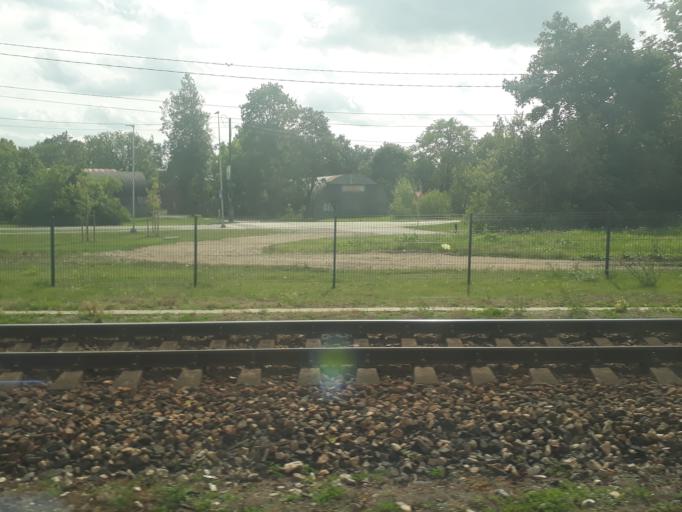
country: EE
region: Laeaene-Virumaa
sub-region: Tapa vald
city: Tapa
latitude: 59.2651
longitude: 25.9585
